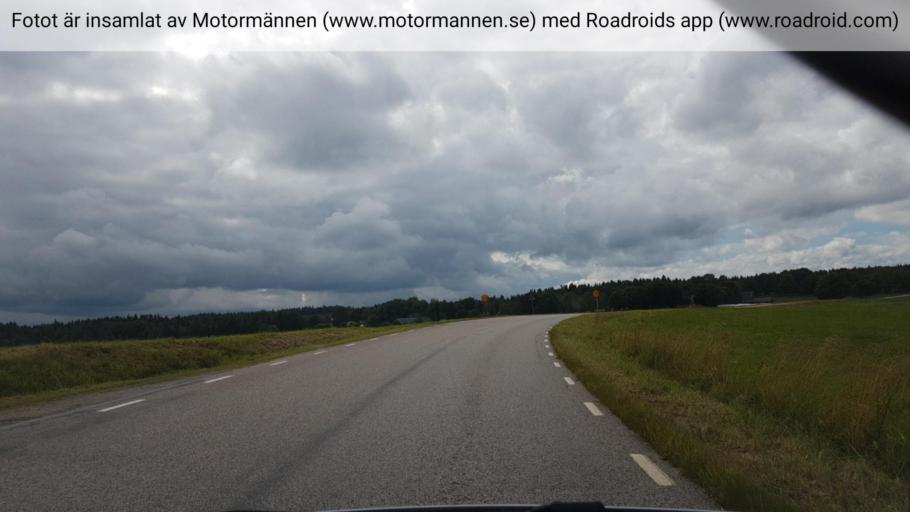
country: SE
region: Vaestra Goetaland
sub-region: Ulricehamns Kommun
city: Ulricehamn
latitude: 57.8000
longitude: 13.5923
